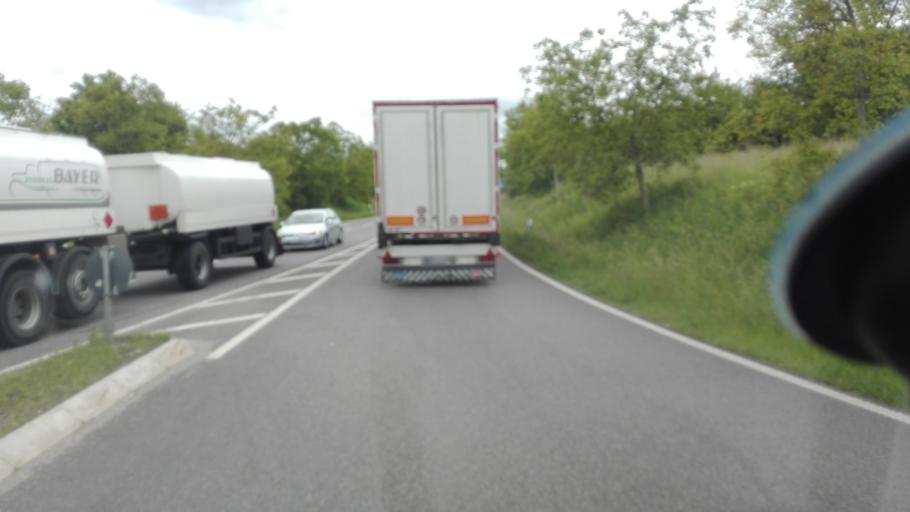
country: DE
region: Baden-Wuerttemberg
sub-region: Karlsruhe Region
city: Ettlingen
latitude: 48.9465
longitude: 8.4969
